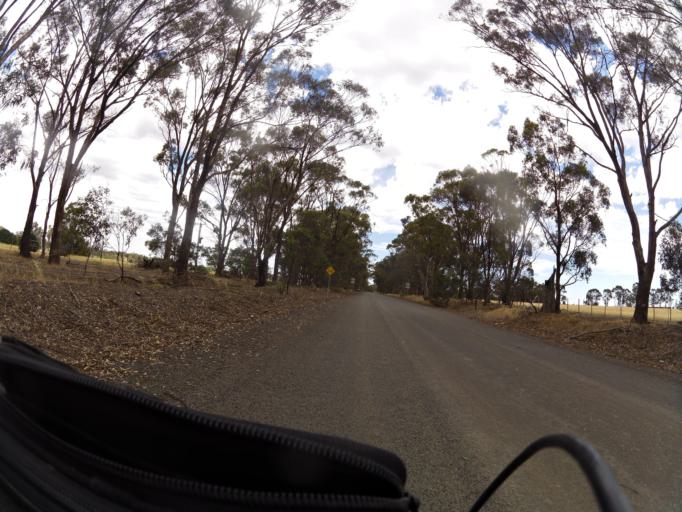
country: AU
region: Victoria
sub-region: Campaspe
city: Kyabram
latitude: -36.7365
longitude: 145.1420
